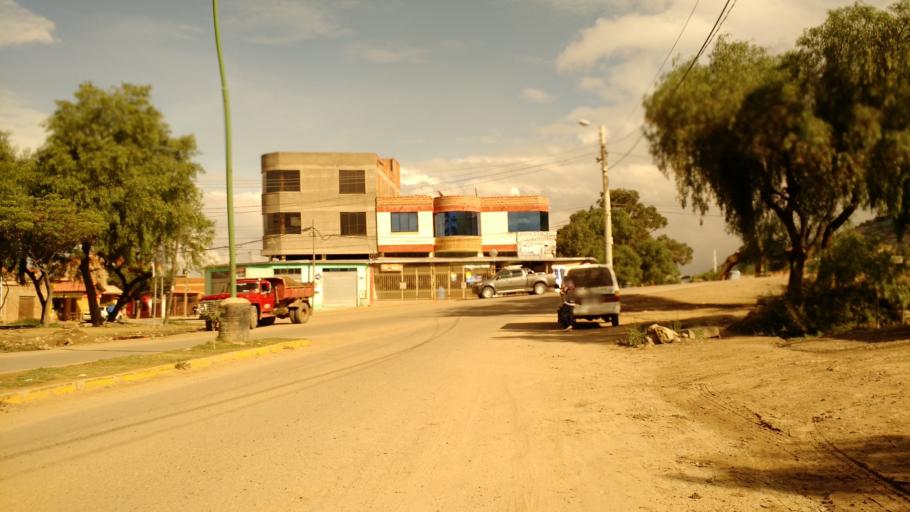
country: BO
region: Cochabamba
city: Cochabamba
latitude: -17.4451
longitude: -66.1414
